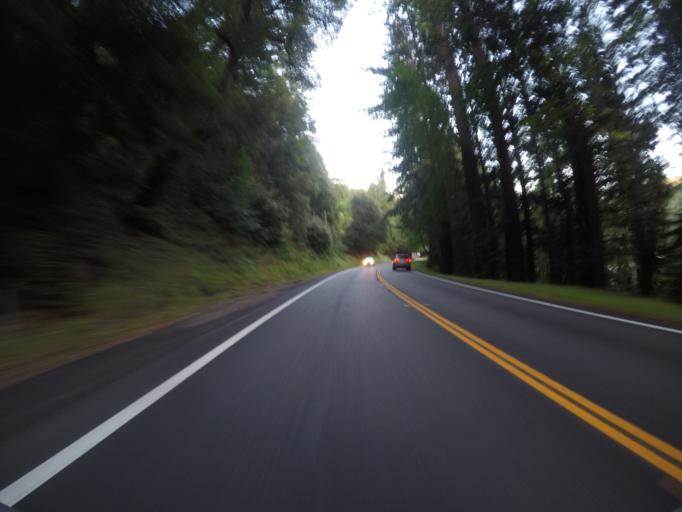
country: US
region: California
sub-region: Humboldt County
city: Redway
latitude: 39.8874
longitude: -123.7388
